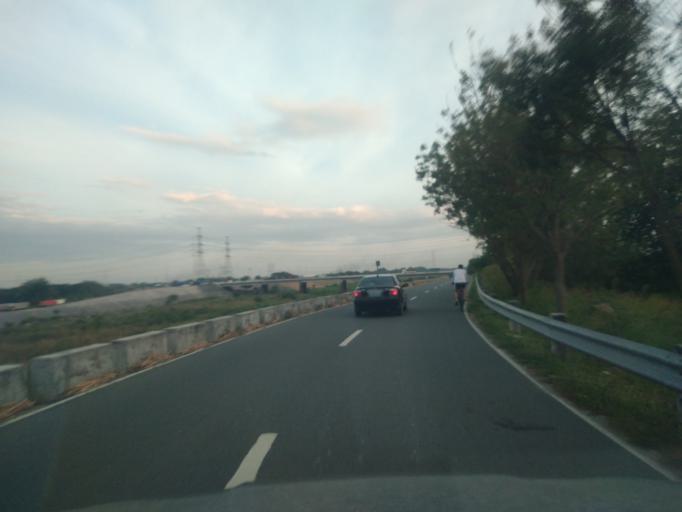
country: PH
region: Central Luzon
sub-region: Province of Pampanga
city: Bacolor
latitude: 15.0001
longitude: 120.6363
